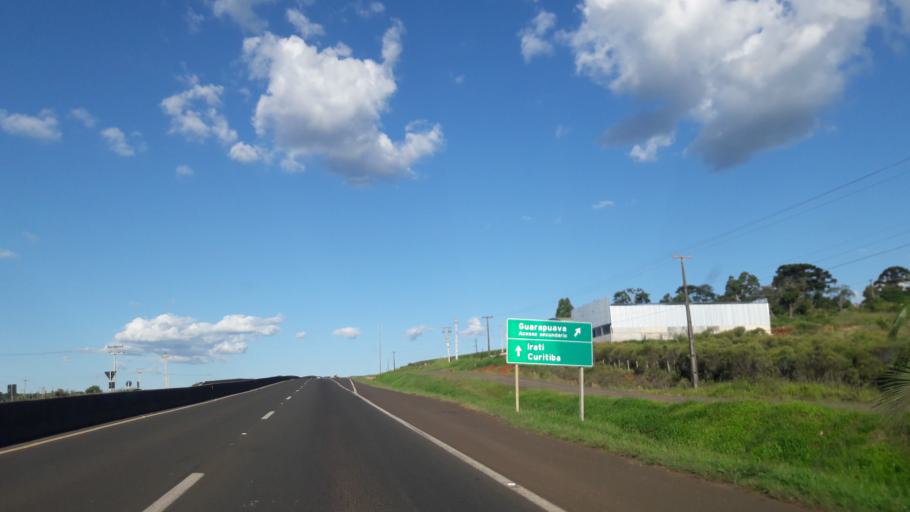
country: BR
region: Parana
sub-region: Guarapuava
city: Guarapuava
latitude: -25.3413
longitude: -51.4325
